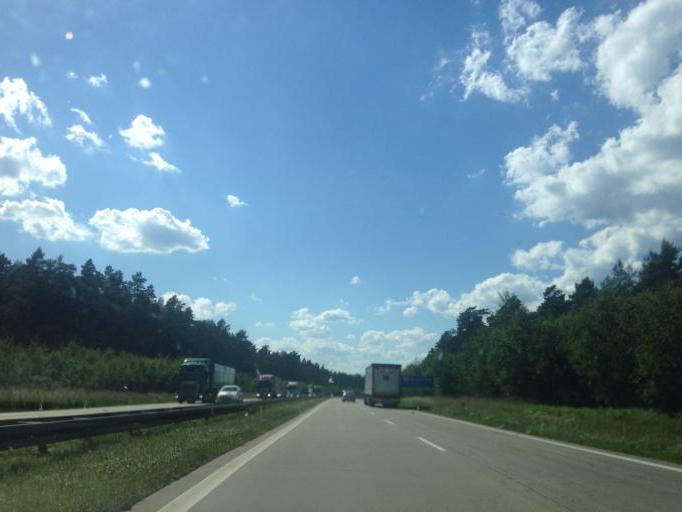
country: PL
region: Lower Silesian Voivodeship
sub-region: Powiat boleslawiecki
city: Gromadka
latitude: 51.3081
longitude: 15.6904
